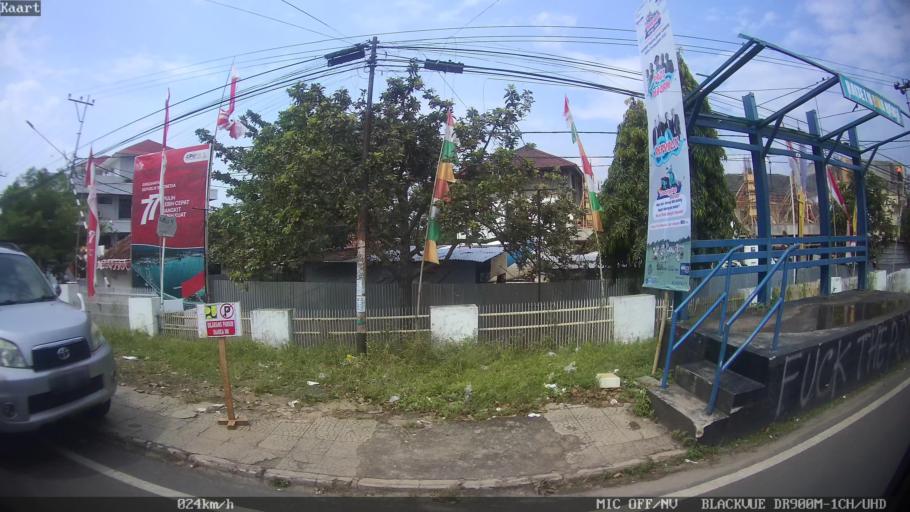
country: ID
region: Lampung
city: Bandarlampung
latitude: -5.4388
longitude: 105.2576
